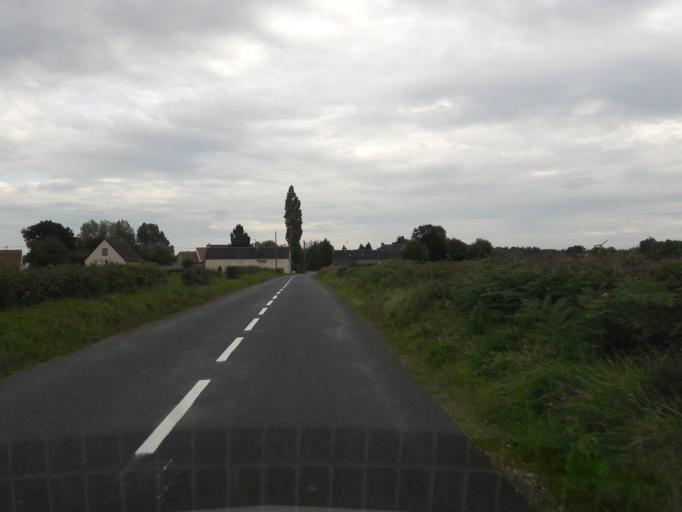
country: FR
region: Lower Normandy
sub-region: Departement du Calvados
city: Bayeux
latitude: 49.1853
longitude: -0.7230
